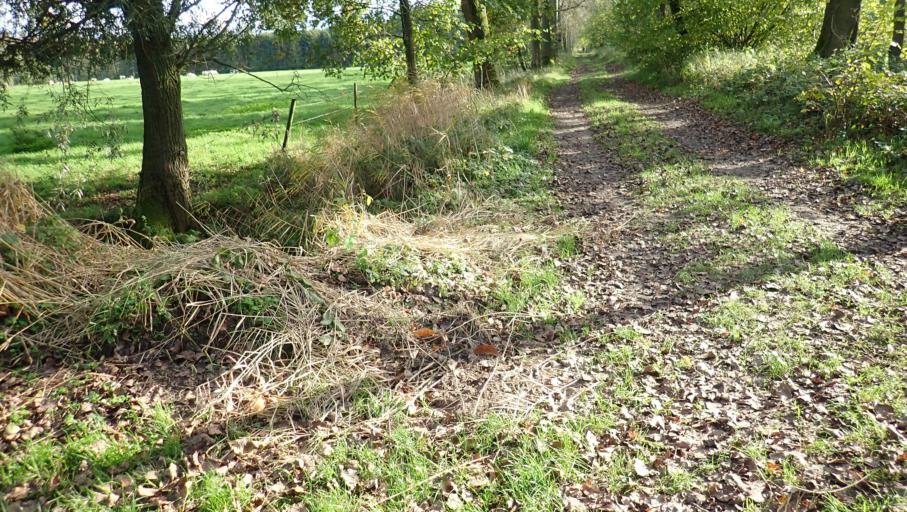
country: BE
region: Flanders
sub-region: Provincie Oost-Vlaanderen
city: Stekene
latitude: 51.1759
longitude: 4.0191
